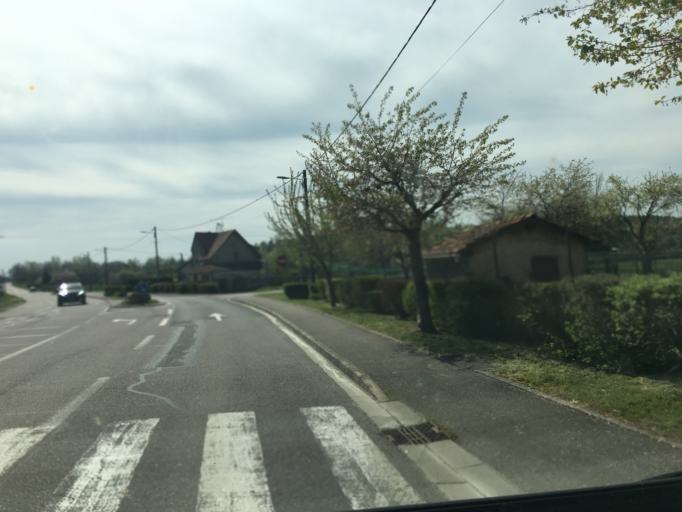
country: FR
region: Lorraine
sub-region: Departement de la Meuse
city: Lerouville
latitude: 48.8221
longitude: 5.5113
